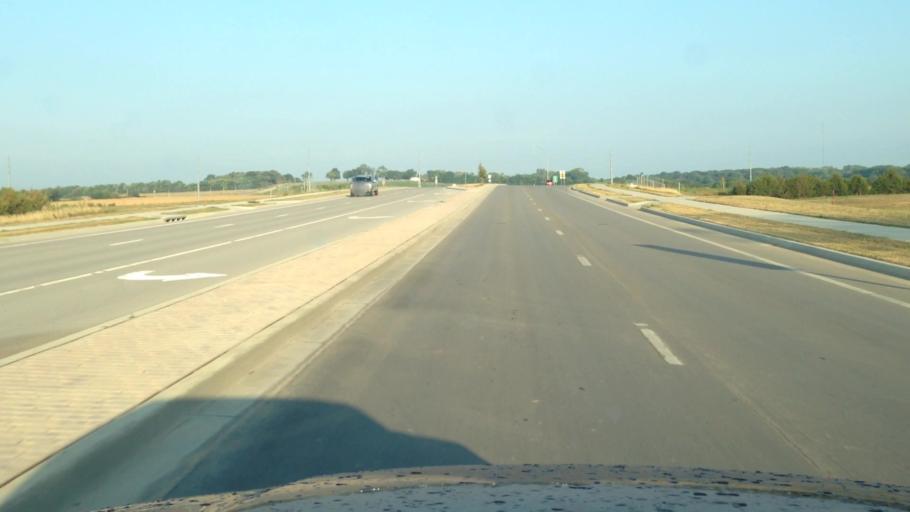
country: US
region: Kansas
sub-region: Douglas County
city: Lawrence
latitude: 38.9601
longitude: -95.3306
